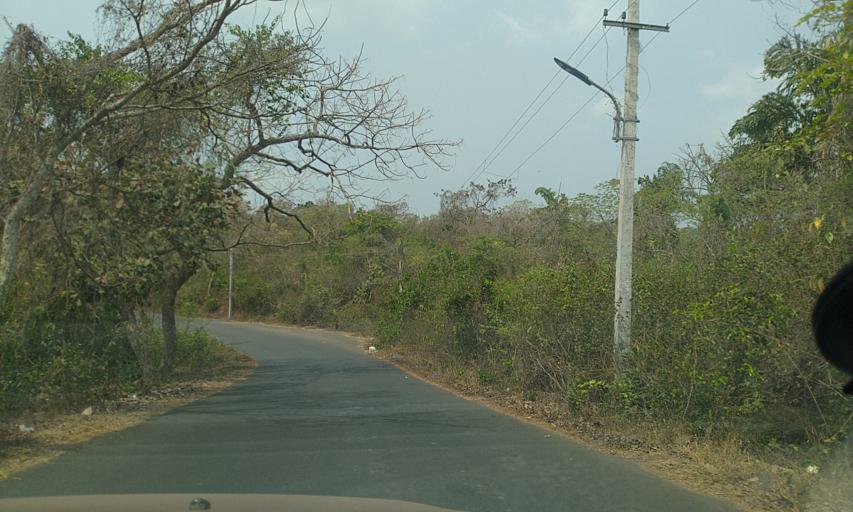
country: IN
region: Goa
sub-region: North Goa
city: Goa Velha
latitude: 15.4807
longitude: 73.8934
